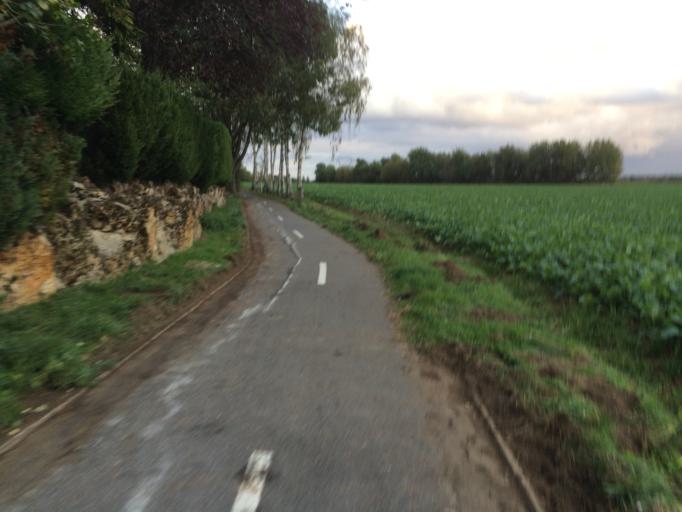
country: FR
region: Ile-de-France
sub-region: Departement de l'Essonne
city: Les Ulis
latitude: 48.6758
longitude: 2.1587
